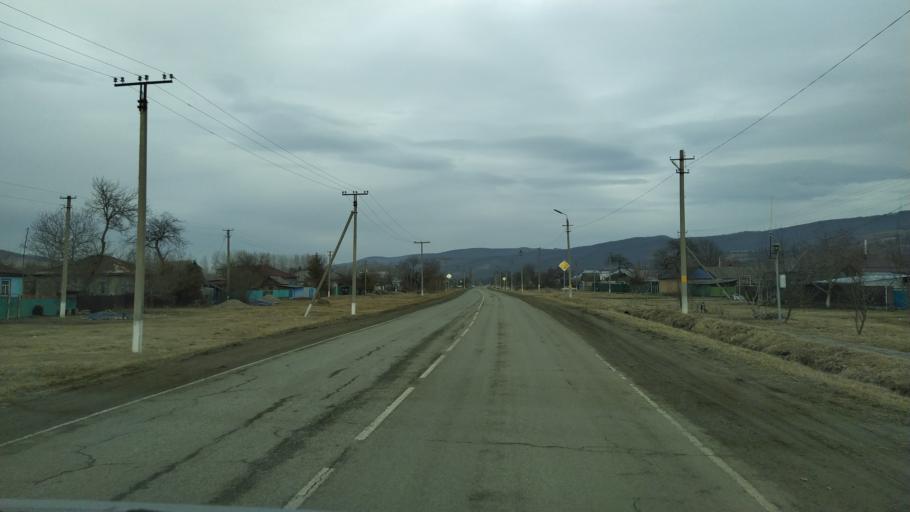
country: RU
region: Krasnodarskiy
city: Peredovaya
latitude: 44.1301
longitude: 41.4878
